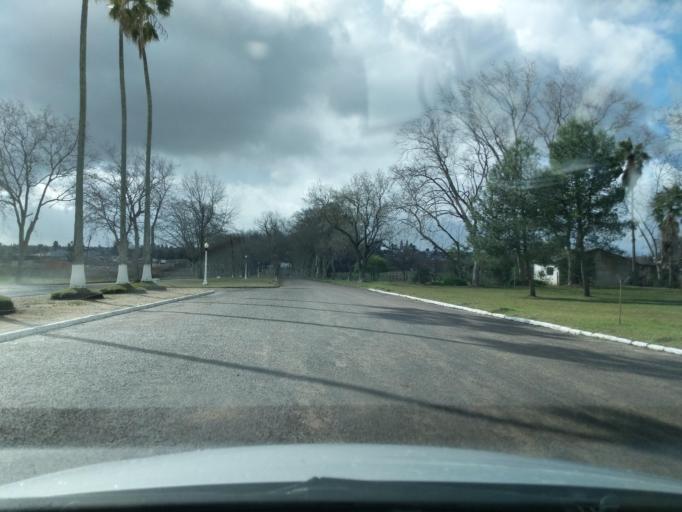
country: UY
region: Florida
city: Florida
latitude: -34.1088
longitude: -56.2286
